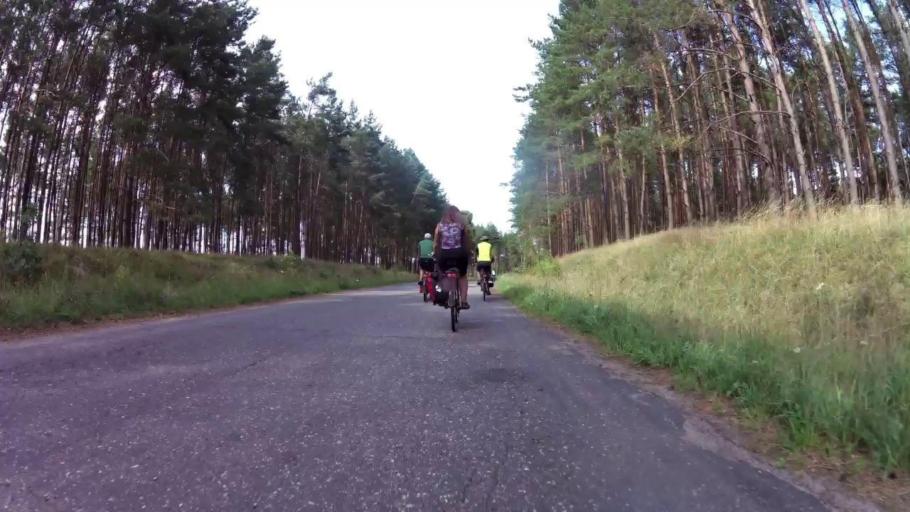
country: PL
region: West Pomeranian Voivodeship
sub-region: Powiat stargardzki
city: Insko
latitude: 53.3966
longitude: 15.5954
